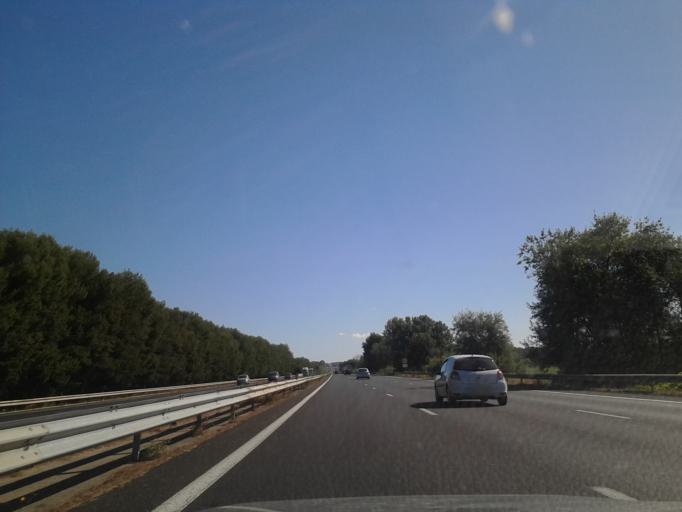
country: FR
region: Languedoc-Roussillon
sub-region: Departement de l'Herault
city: Villeneuve-les-Beziers
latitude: 43.3153
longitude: 3.2585
